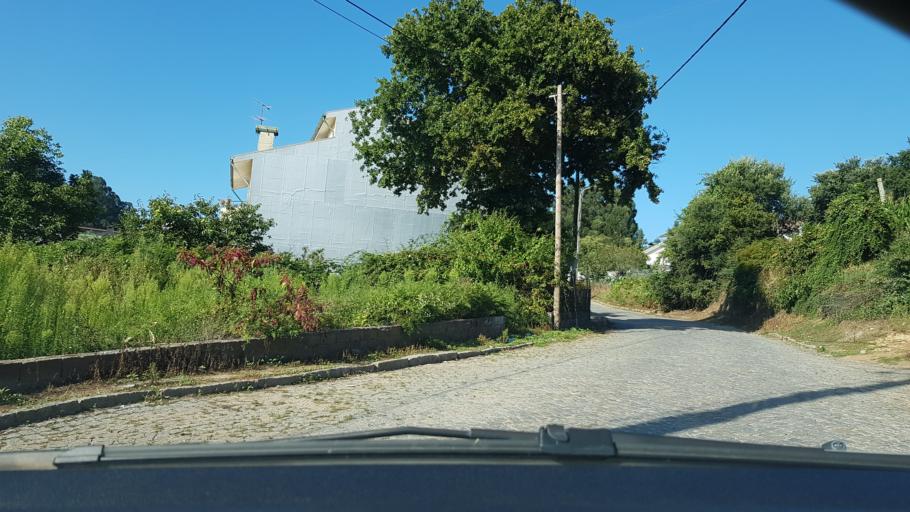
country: PT
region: Porto
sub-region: Gondomar
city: Baguim do Monte
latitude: 41.1873
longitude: -8.5319
